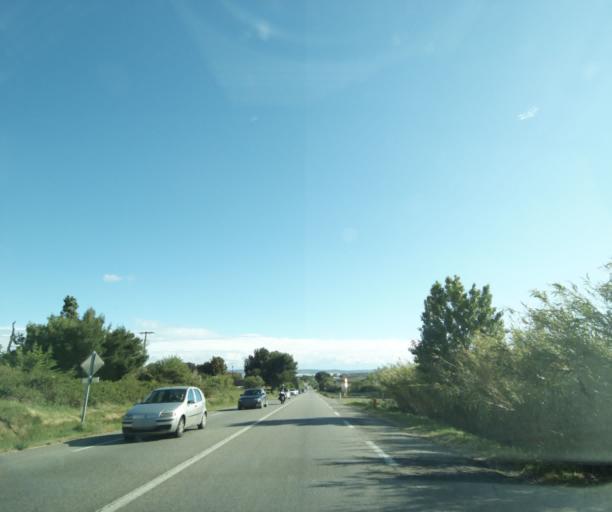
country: FR
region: Provence-Alpes-Cote d'Azur
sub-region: Departement des Bouches-du-Rhone
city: Vitrolles
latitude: 43.4561
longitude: 5.2324
